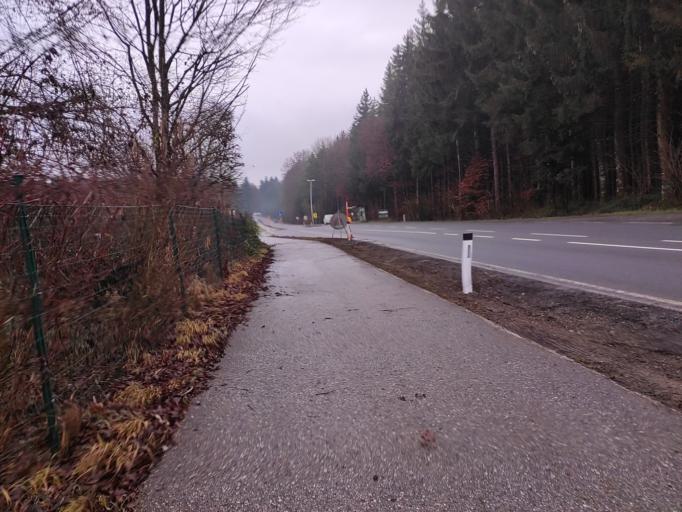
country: AT
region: Salzburg
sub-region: Politischer Bezirk Salzburg-Umgebung
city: Seekirchen am Wallersee
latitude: 47.9129
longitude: 13.1105
